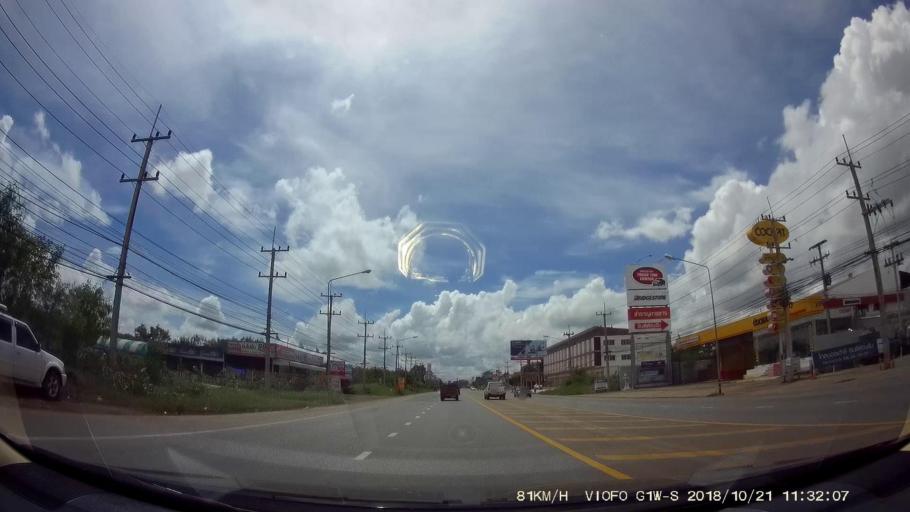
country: TH
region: Chaiyaphum
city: Chaiyaphum
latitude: 15.7622
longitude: 102.0248
